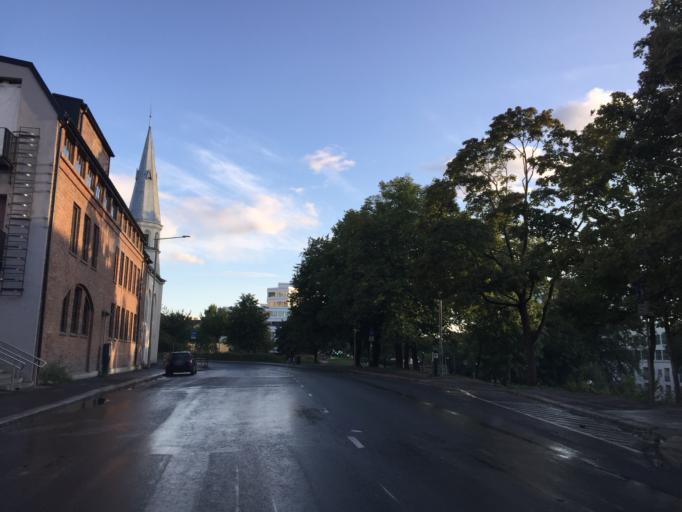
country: NO
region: Oslo
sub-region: Oslo
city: Oslo
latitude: 59.9171
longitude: 10.7624
